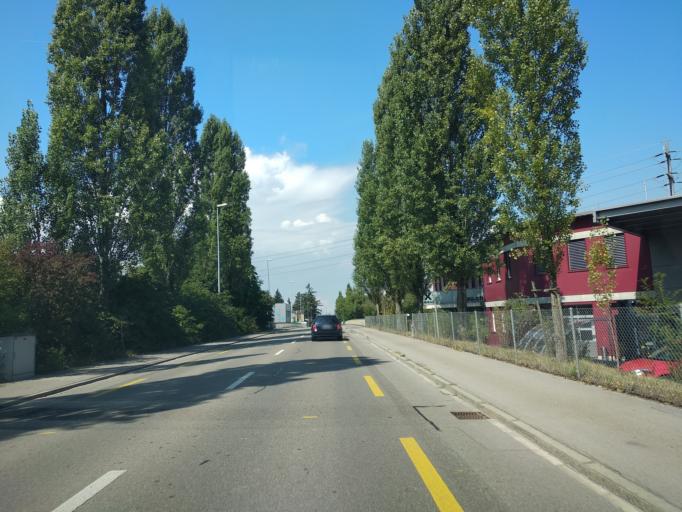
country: CH
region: Thurgau
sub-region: Frauenfeld District
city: Frauenfeld
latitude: 47.5630
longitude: 8.8781
